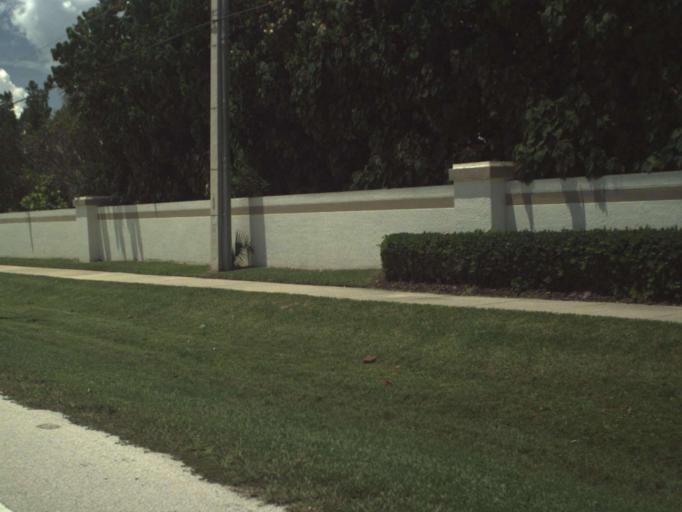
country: US
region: Florida
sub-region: Martin County
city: Sewall's Point
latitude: 27.2312
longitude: -80.1846
